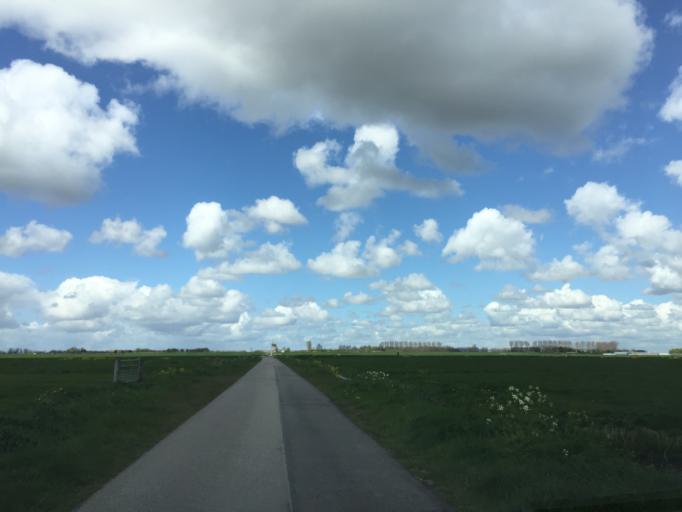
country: NL
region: South Holland
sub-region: Gemeente Kaag en Braassem
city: Oude Wetering
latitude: 52.2020
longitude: 4.6045
